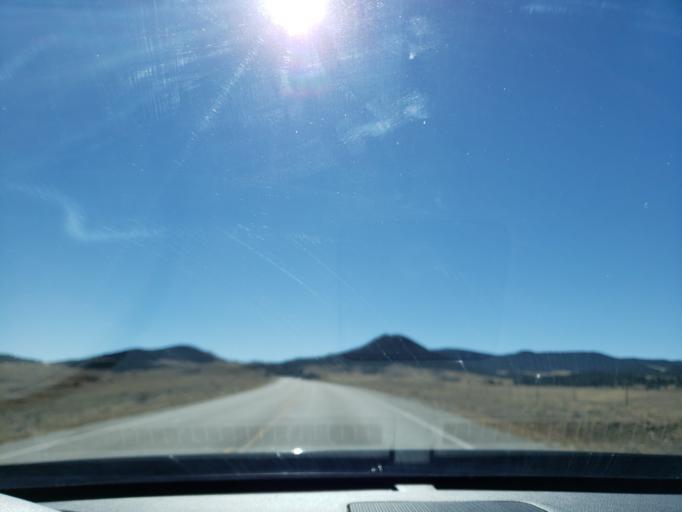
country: US
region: Colorado
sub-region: Chaffee County
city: Salida
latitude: 38.8554
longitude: -105.6534
